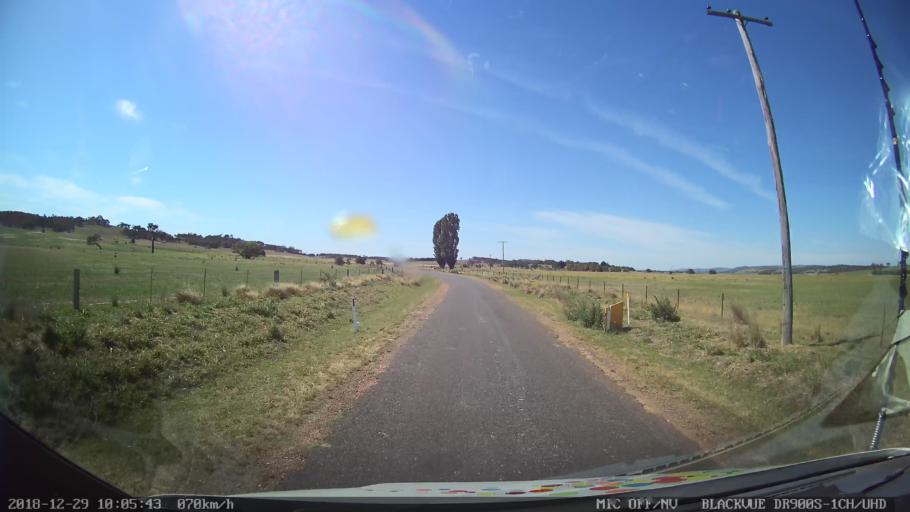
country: AU
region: New South Wales
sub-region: Goulburn Mulwaree
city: Goulburn
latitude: -34.8360
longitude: 149.4537
